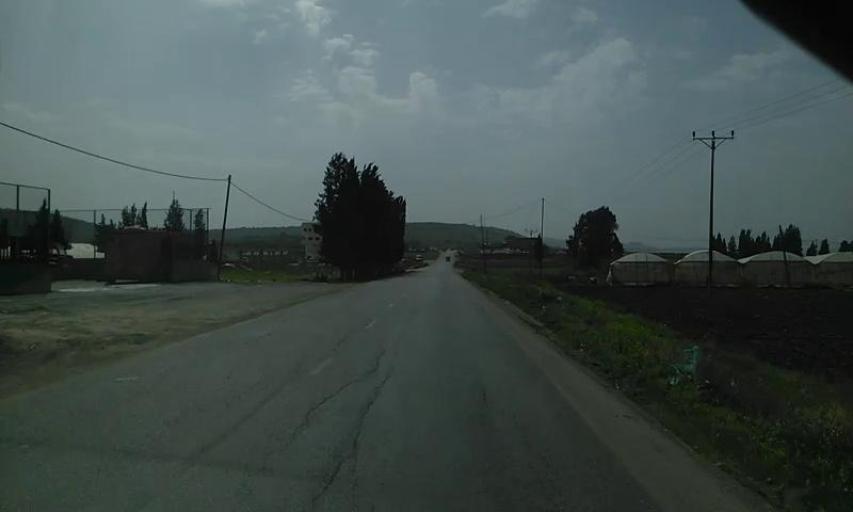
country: PS
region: West Bank
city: Ash Shuhada'
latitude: 32.4271
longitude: 35.2567
